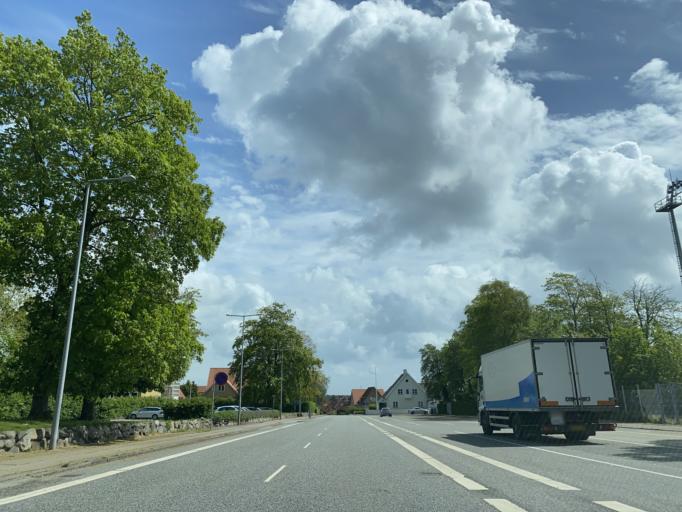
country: DK
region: South Denmark
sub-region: Sonderborg Kommune
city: Sonderborg
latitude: 54.9062
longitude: 9.7987
